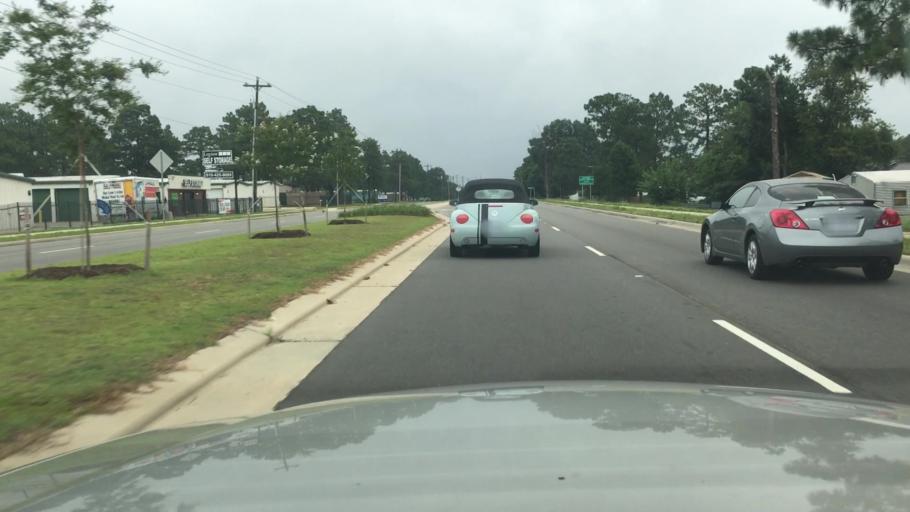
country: US
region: North Carolina
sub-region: Cumberland County
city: Hope Mills
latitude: 35.0100
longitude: -78.9108
